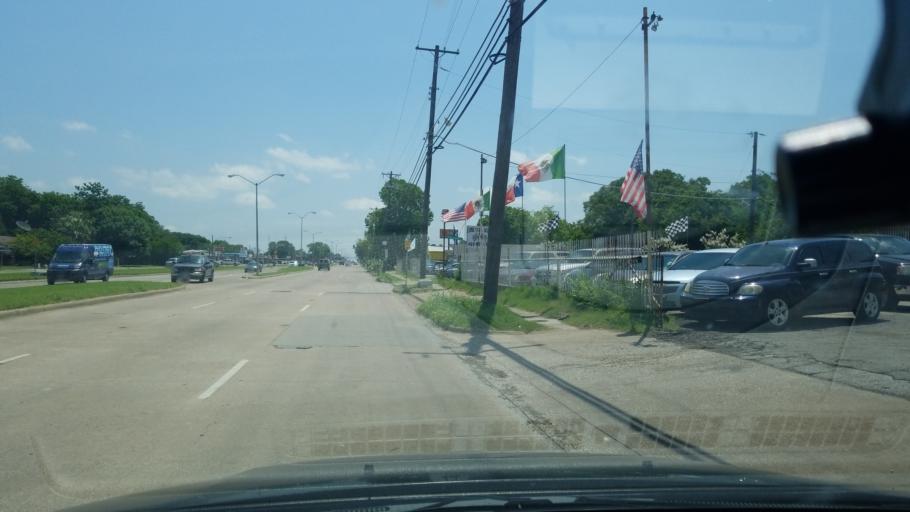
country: US
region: Texas
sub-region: Dallas County
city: Balch Springs
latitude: 32.7342
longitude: -96.6907
